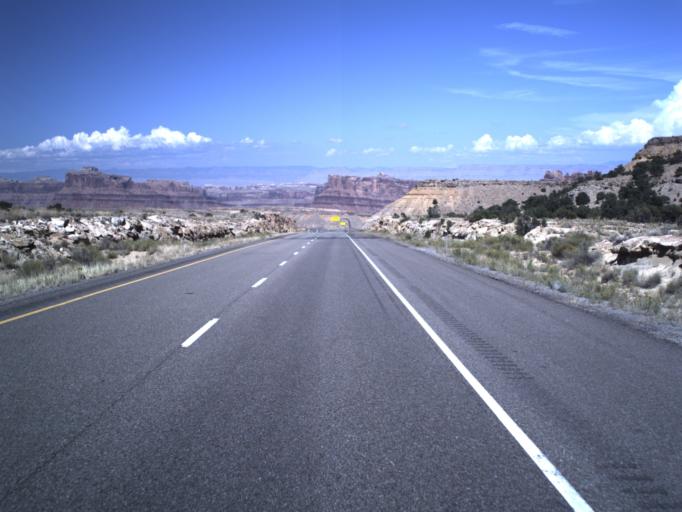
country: US
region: Utah
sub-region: Emery County
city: Castle Dale
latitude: 38.9216
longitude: -110.4999
